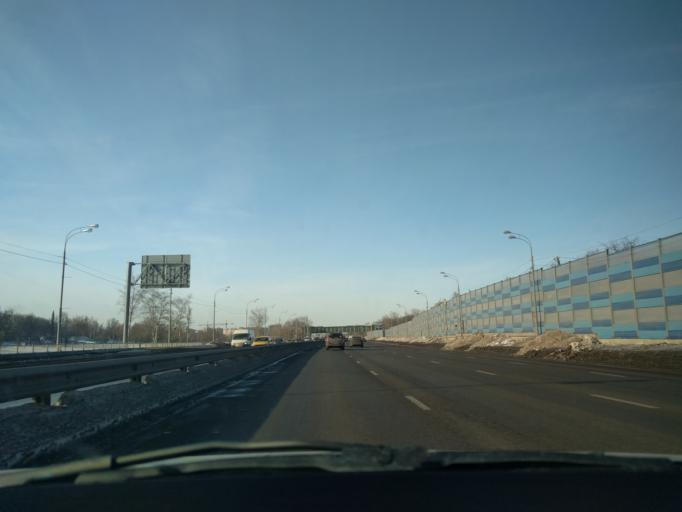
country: RU
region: Moscow
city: Severnyy
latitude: 55.9392
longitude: 37.5448
